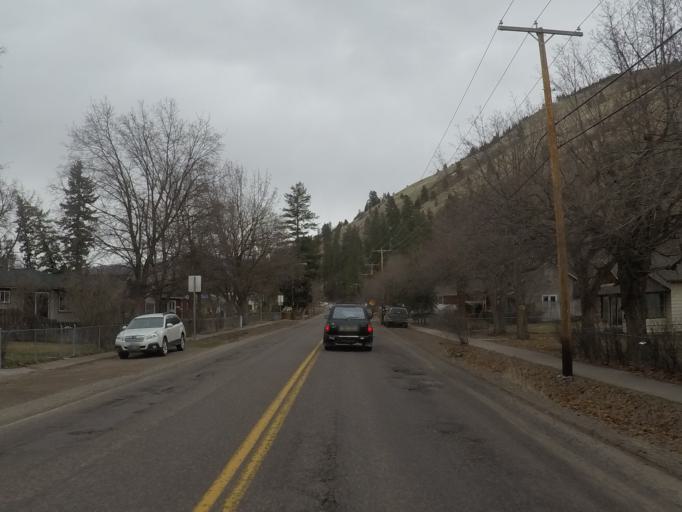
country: US
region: Montana
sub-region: Missoula County
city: Missoula
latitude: 46.8760
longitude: -113.9732
